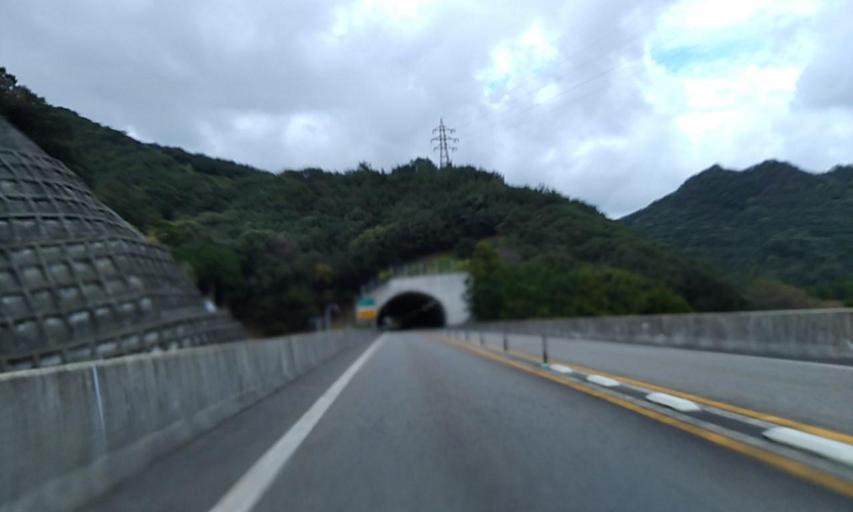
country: JP
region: Wakayama
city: Shingu
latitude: 33.6285
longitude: 135.9220
